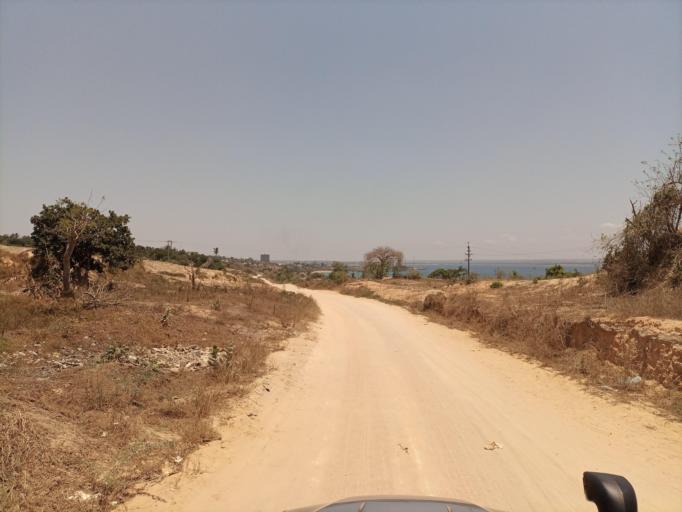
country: MZ
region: Nampula
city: Nacala
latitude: -14.5194
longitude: 40.6799
